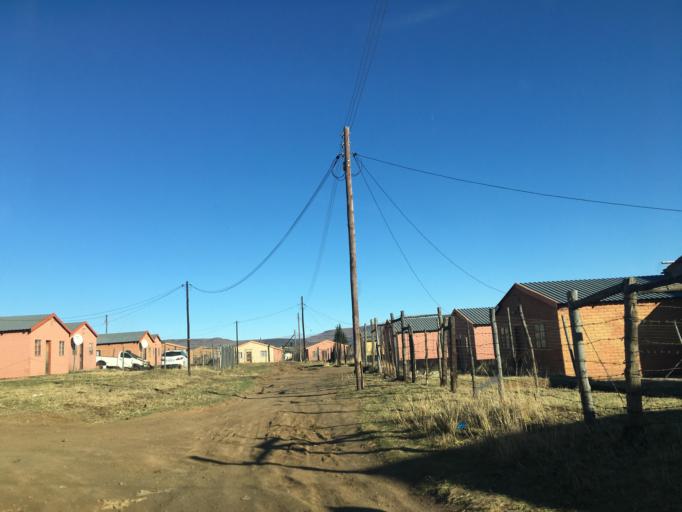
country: ZA
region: Eastern Cape
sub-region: Chris Hani District Municipality
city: Cala
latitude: -31.5390
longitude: 27.6832
